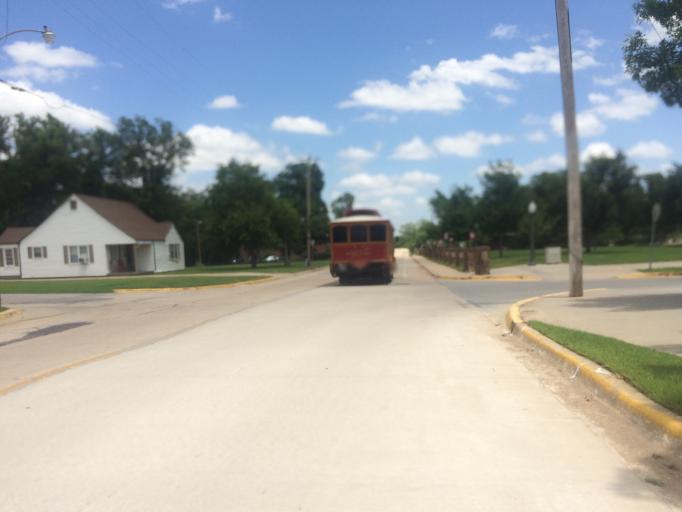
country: US
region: Oklahoma
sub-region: Cleveland County
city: Norman
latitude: 35.2075
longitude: -97.4404
